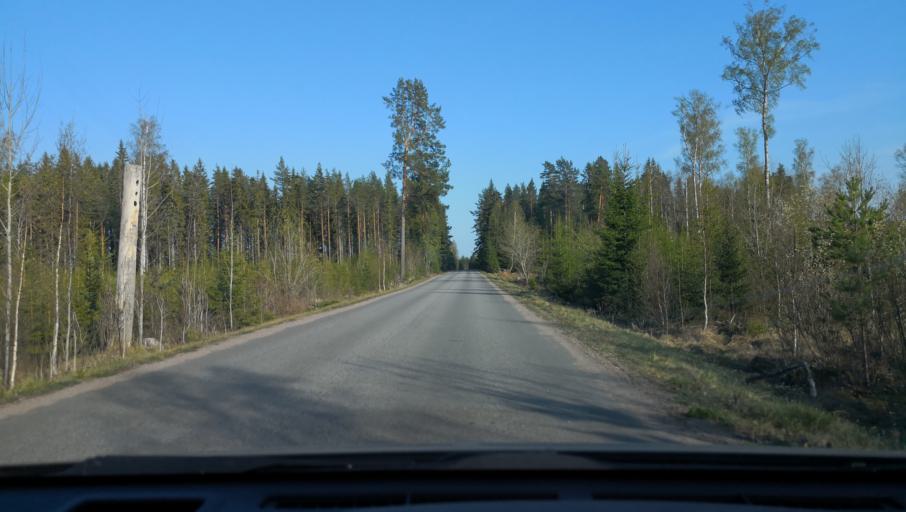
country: SE
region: Uppsala
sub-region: Heby Kommun
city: Tarnsjo
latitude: 60.2618
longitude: 16.9350
